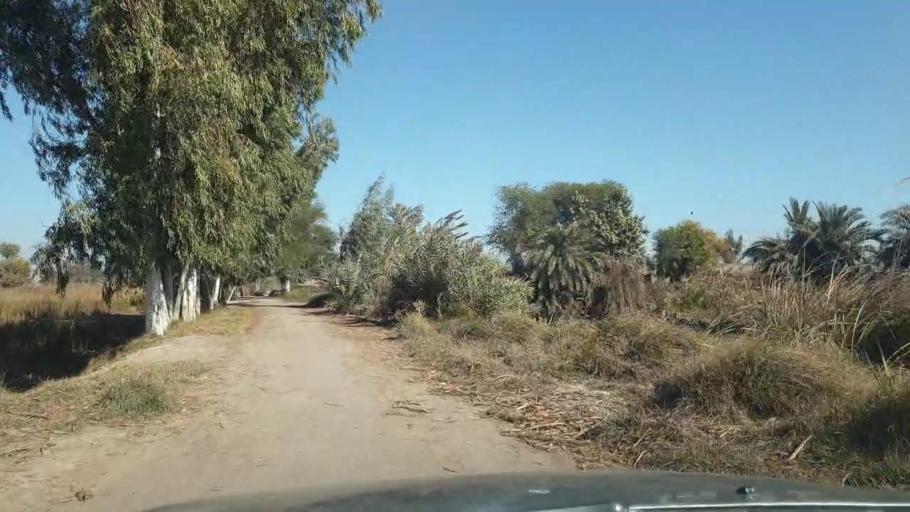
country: PK
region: Sindh
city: Ghotki
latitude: 28.0334
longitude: 69.2888
